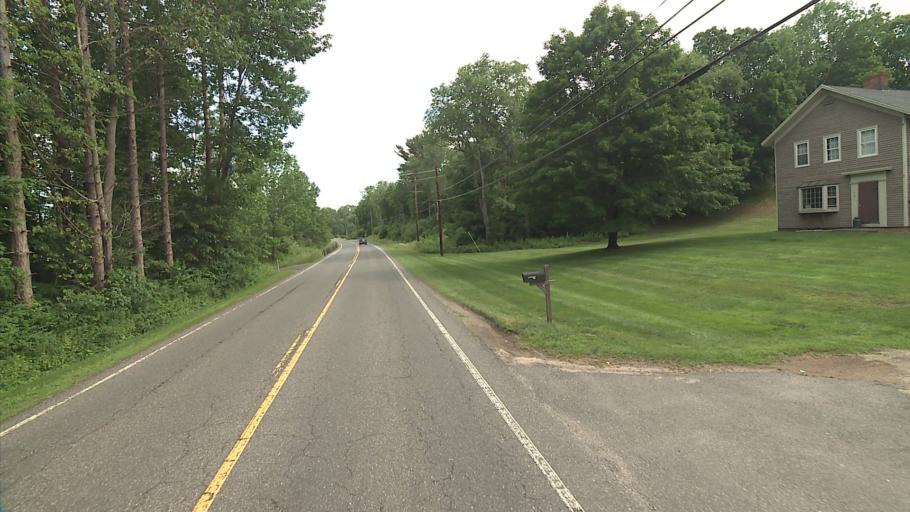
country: US
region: Connecticut
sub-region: Litchfield County
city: Litchfield
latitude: 41.7268
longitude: -73.1856
